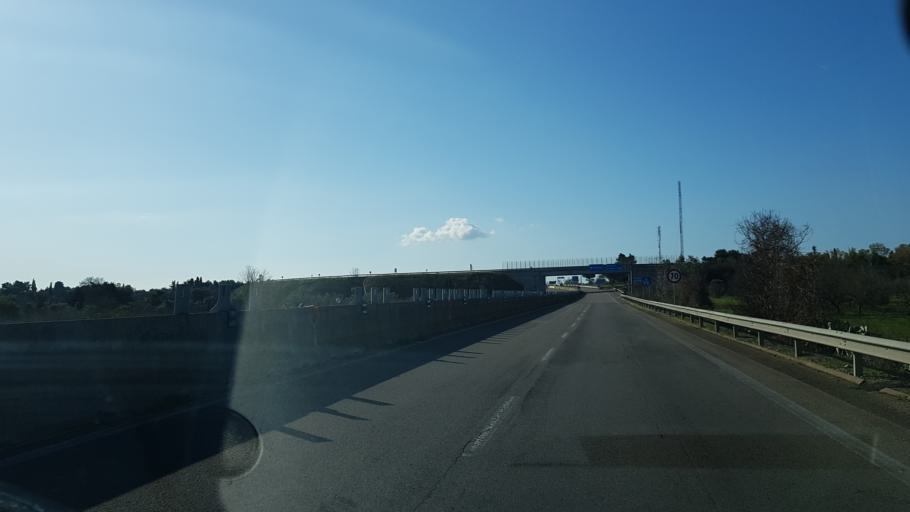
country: IT
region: Apulia
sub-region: Provincia di Lecce
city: Sannicola
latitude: 40.1025
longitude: 18.0323
